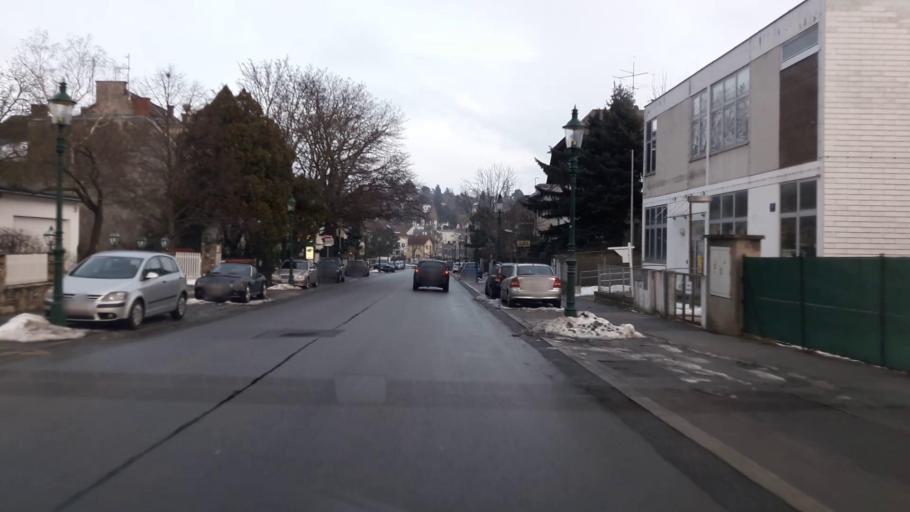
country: AT
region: Lower Austria
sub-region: Politischer Bezirk Wien-Umgebung
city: Klosterneuburg
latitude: 48.2508
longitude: 16.3050
